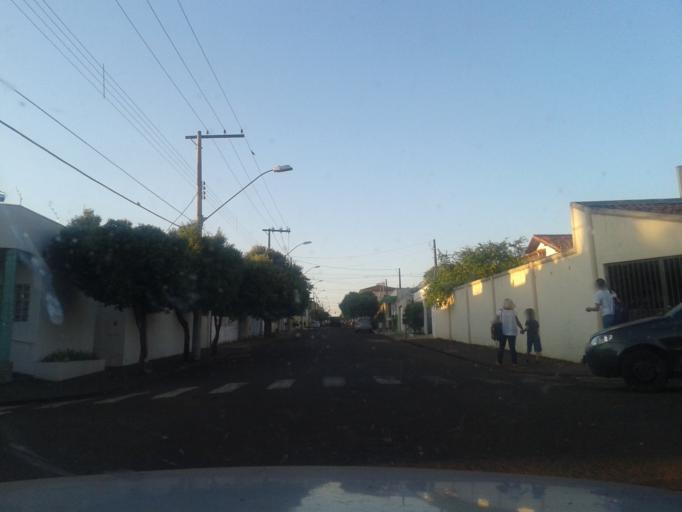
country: BR
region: Minas Gerais
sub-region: Ituiutaba
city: Ituiutaba
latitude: -18.9802
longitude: -49.4648
